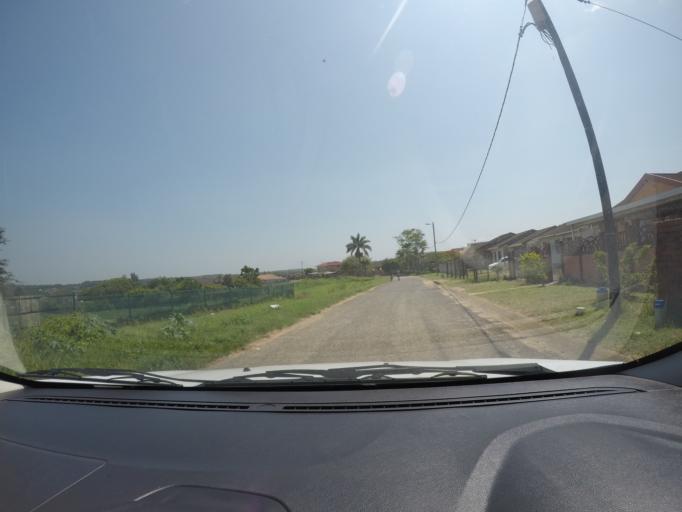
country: ZA
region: KwaZulu-Natal
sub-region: uThungulu District Municipality
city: eSikhawini
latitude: -28.8675
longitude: 31.9227
